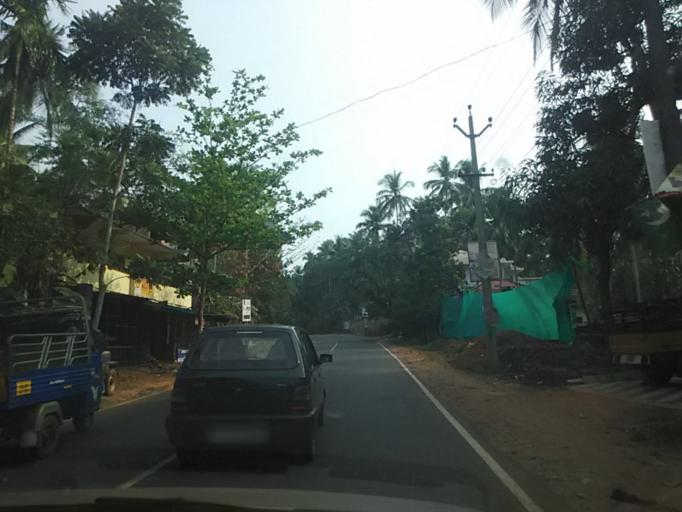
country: IN
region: Kerala
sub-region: Kozhikode
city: Naduvannur
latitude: 11.4939
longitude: 75.7747
